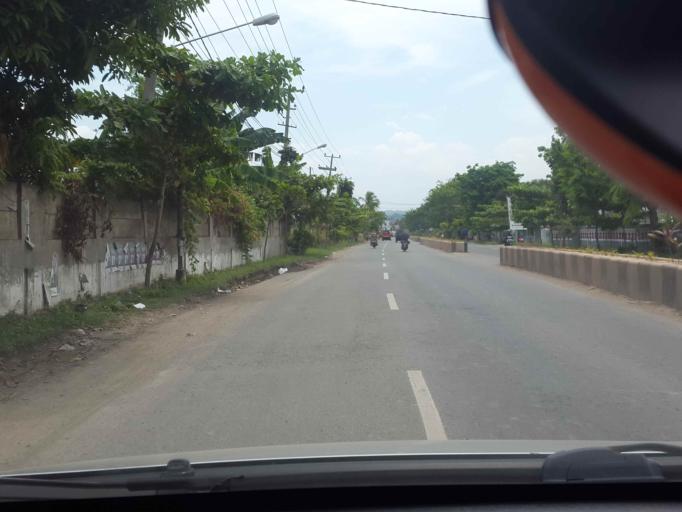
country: ID
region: Lampung
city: Panjang
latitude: -5.4469
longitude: 105.2982
